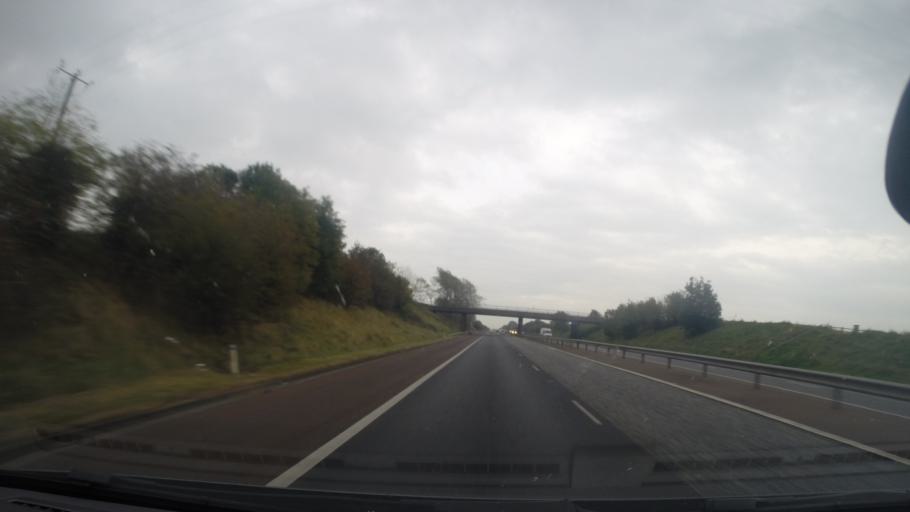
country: GB
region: Northern Ireland
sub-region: Armagh District
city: Portadown
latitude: 54.4753
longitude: -6.4800
